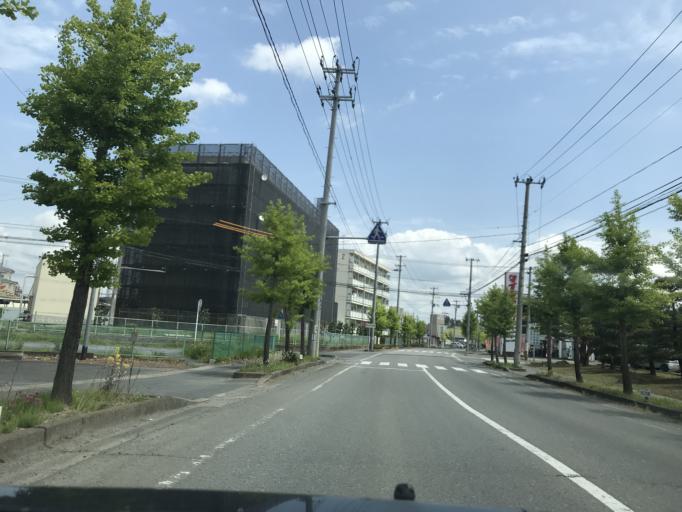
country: JP
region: Miyagi
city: Wakuya
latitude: 38.6927
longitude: 141.1877
